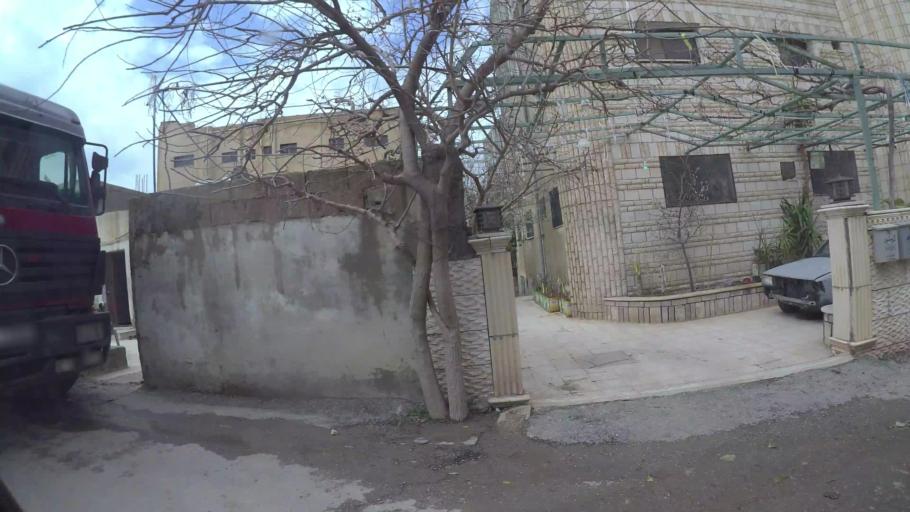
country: JO
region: Amman
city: Al Jubayhah
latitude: 32.0518
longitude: 35.8307
